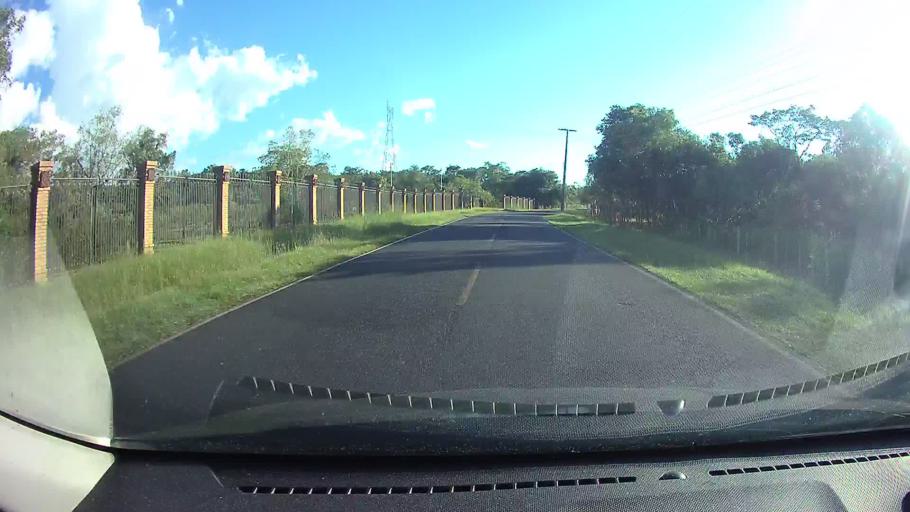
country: PY
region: Cordillera
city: Emboscada
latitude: -25.1778
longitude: -57.2906
